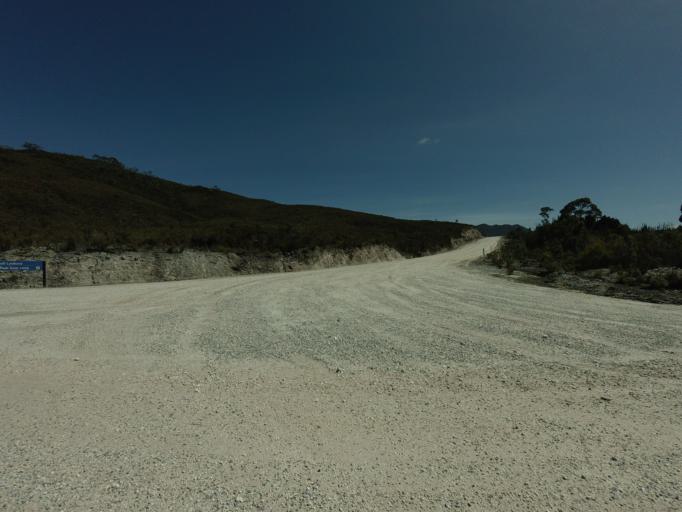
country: AU
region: Tasmania
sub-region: Huon Valley
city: Geeveston
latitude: -43.0337
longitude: 146.2930
